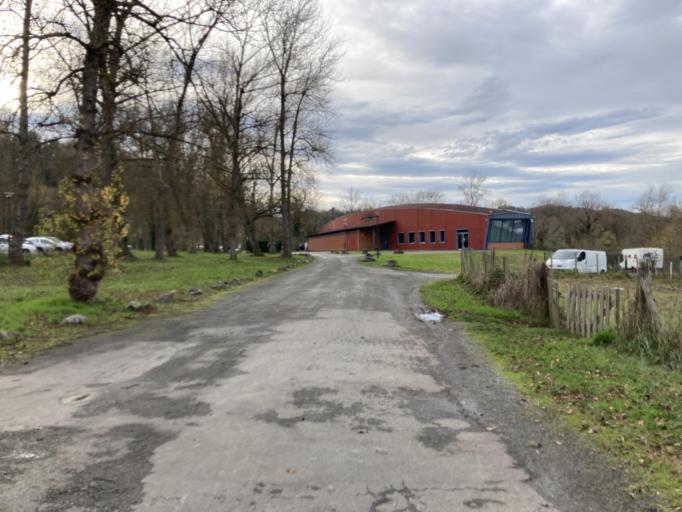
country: FR
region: Aquitaine
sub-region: Departement des Pyrenees-Atlantiques
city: Lescar
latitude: 43.3067
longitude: -0.4336
